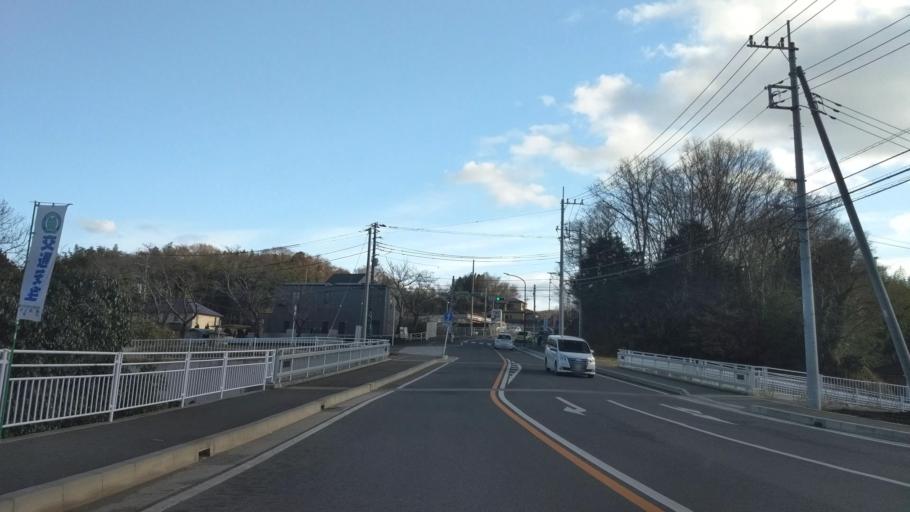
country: JP
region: Kanagawa
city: Hadano
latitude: 35.3498
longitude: 139.2608
